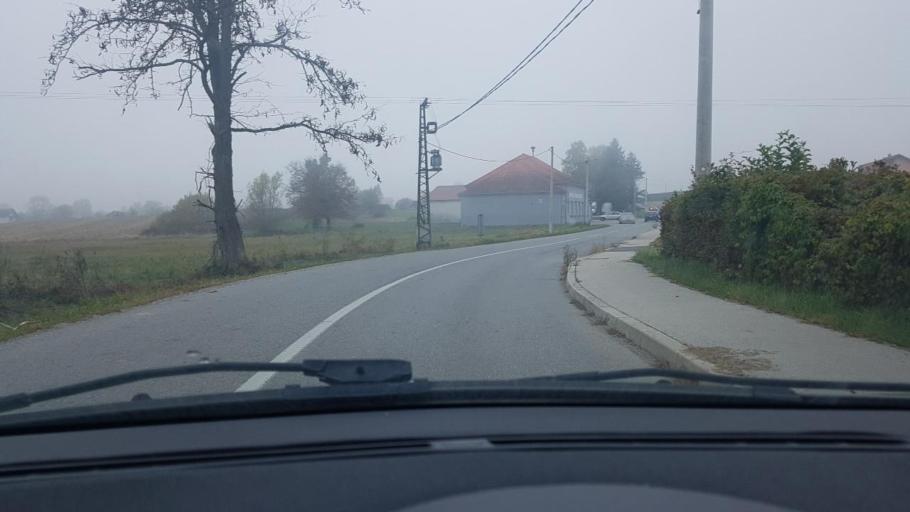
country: HR
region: Krapinsko-Zagorska
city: Marija Bistrica
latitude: 46.0577
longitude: 16.1702
